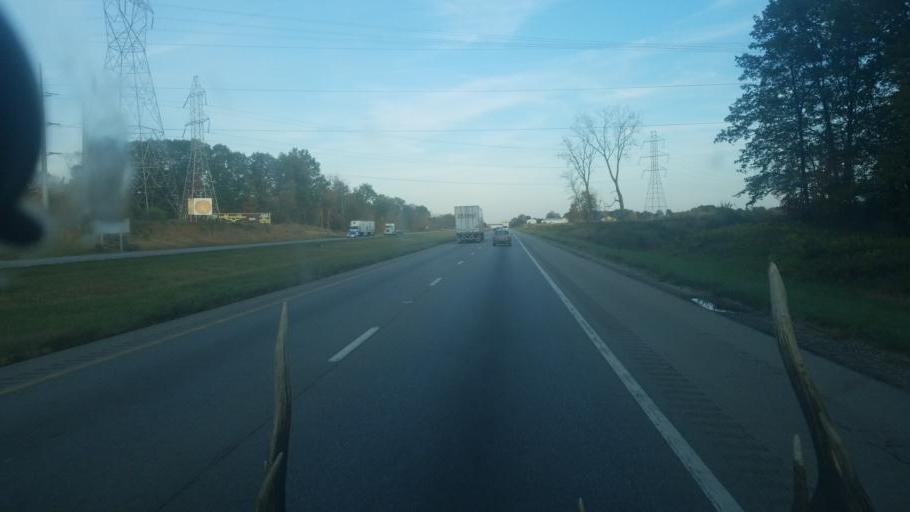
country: US
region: Ohio
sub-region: Licking County
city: Etna
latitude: 39.9474
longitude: -82.6596
